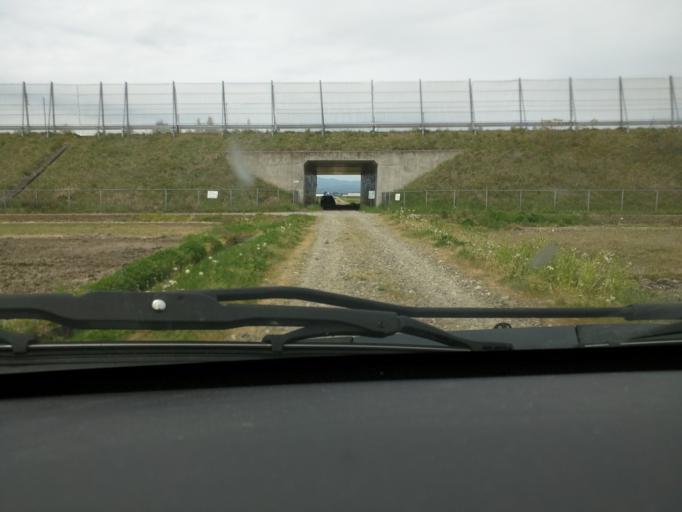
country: JP
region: Fukushima
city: Kitakata
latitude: 37.5297
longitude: 139.8654
